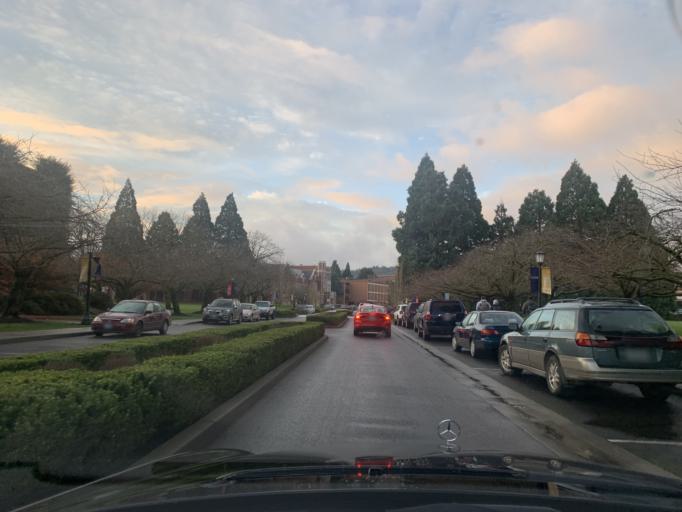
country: US
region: Oregon
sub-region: Multnomah County
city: Portland
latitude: 45.5742
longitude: -122.7244
